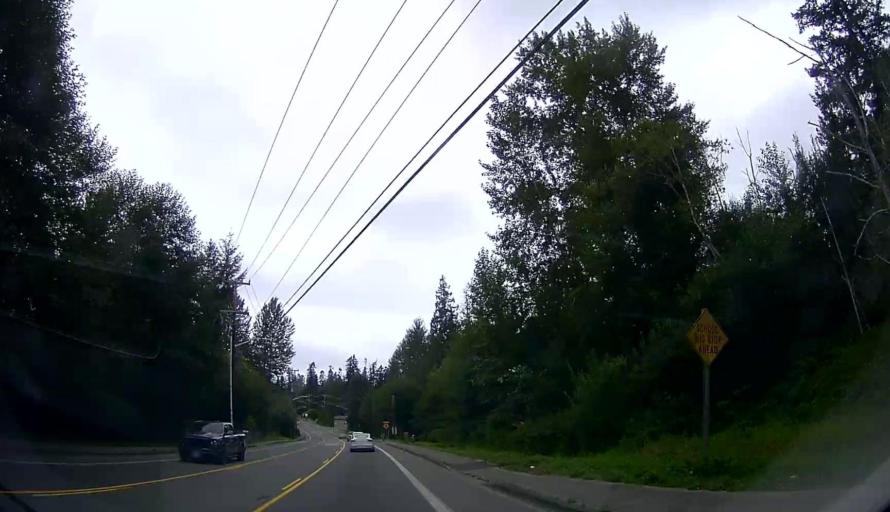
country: US
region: Washington
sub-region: Snohomish County
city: Marysville
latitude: 48.0517
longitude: -122.2101
